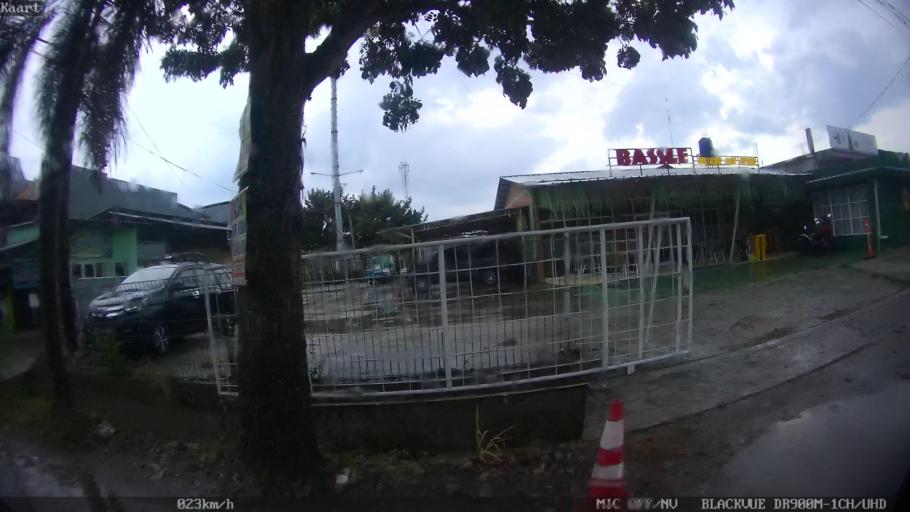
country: ID
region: Lampung
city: Kedaton
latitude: -5.3901
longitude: 105.2940
